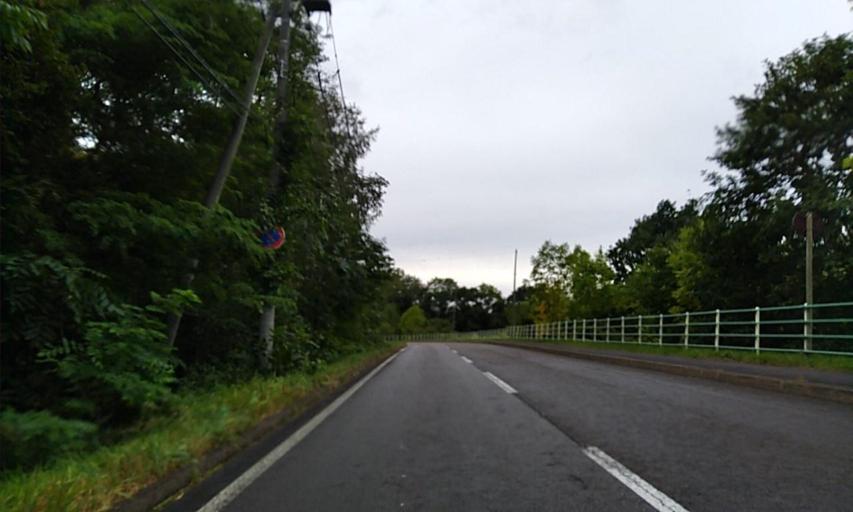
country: JP
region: Hokkaido
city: Abashiri
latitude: 43.9993
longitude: 144.2291
